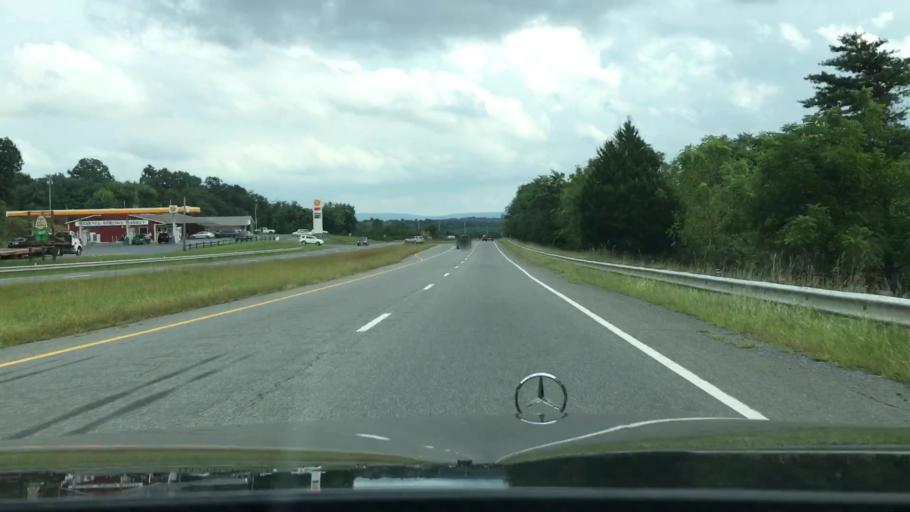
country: US
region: Virginia
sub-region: Frederick County
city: Shawnee Land
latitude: 39.3183
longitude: -78.2945
